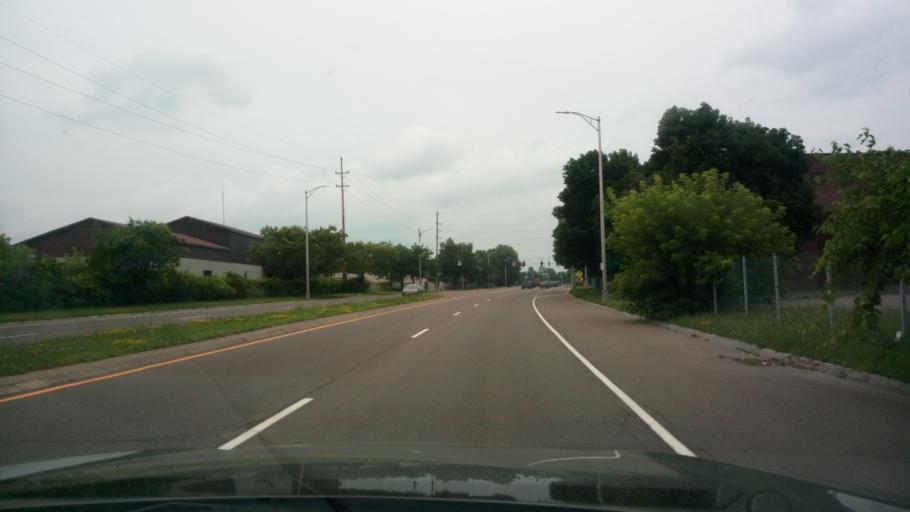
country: US
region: New York
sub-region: Chemung County
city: Elmira
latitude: 42.0957
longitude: -76.8072
